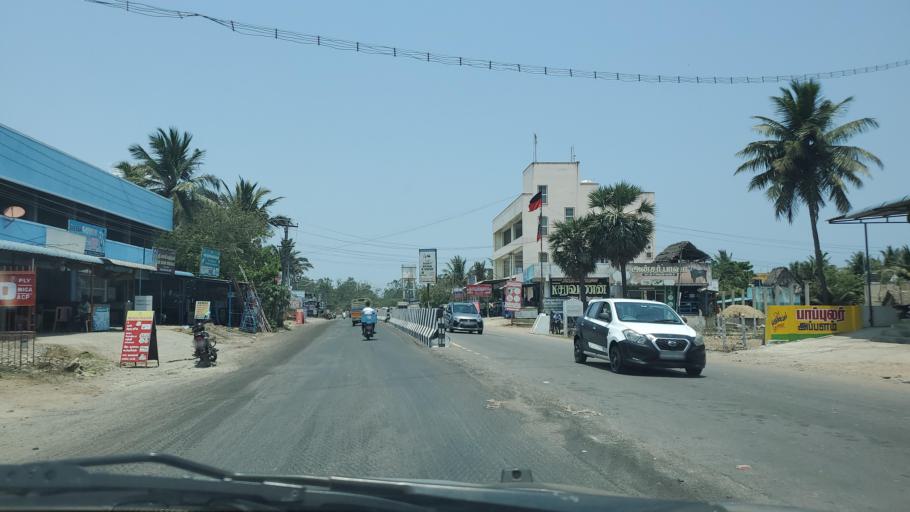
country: IN
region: Tamil Nadu
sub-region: Kancheepuram
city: Vengavasal
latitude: 12.8652
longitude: 80.1757
